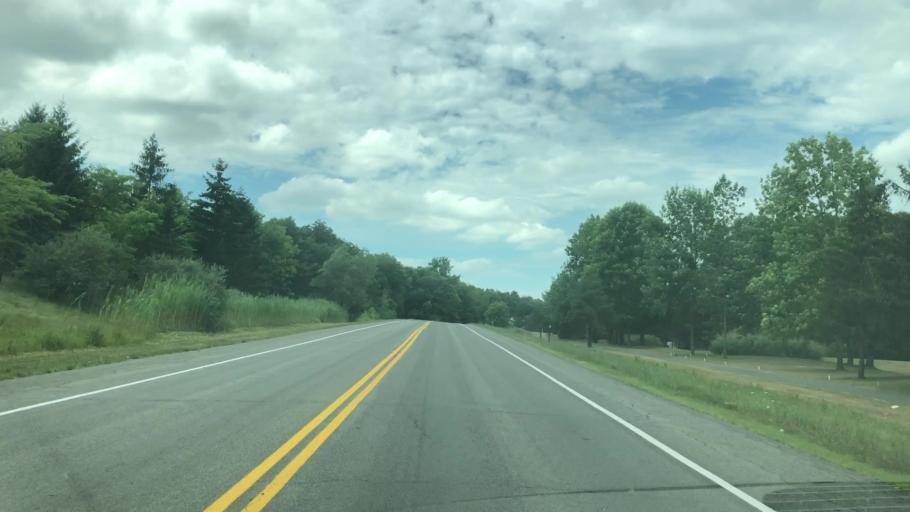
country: US
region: New York
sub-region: Wayne County
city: Macedon
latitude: 43.1237
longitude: -77.3329
